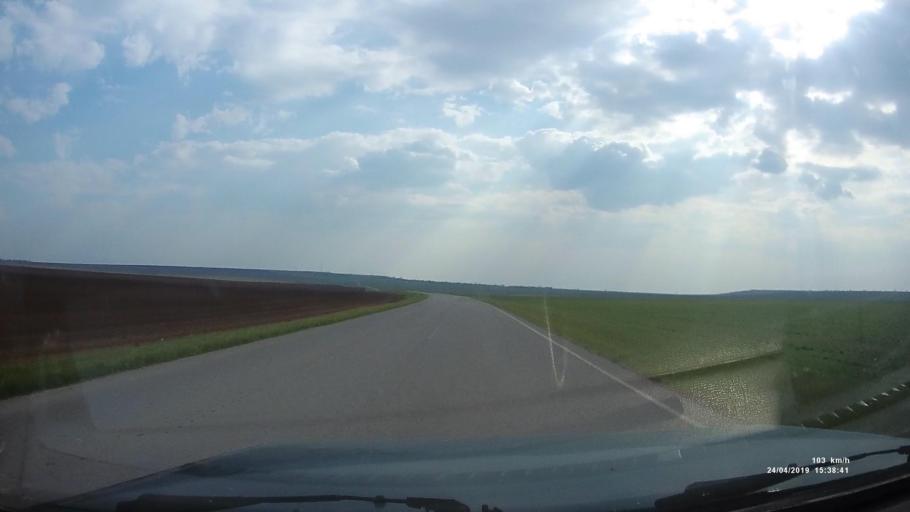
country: RU
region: Kalmykiya
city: Yashalta
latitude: 46.5952
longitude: 42.8241
